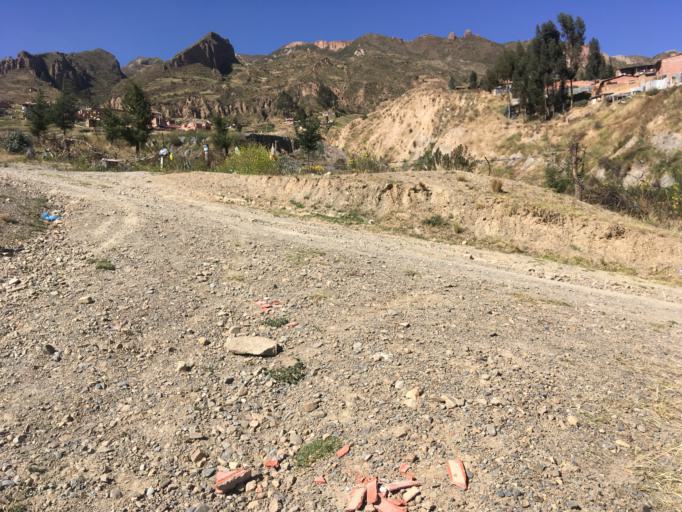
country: BO
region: La Paz
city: La Paz
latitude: -16.5438
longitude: -68.0399
